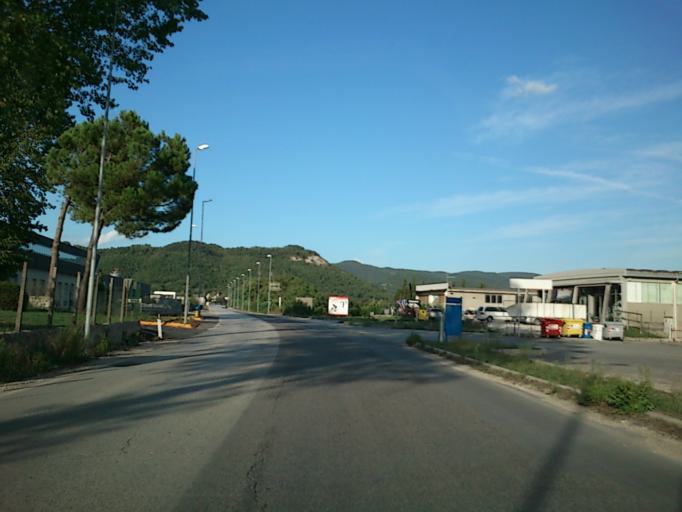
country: IT
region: The Marches
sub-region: Provincia di Pesaro e Urbino
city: Fermignano
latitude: 43.6907
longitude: 12.6537
